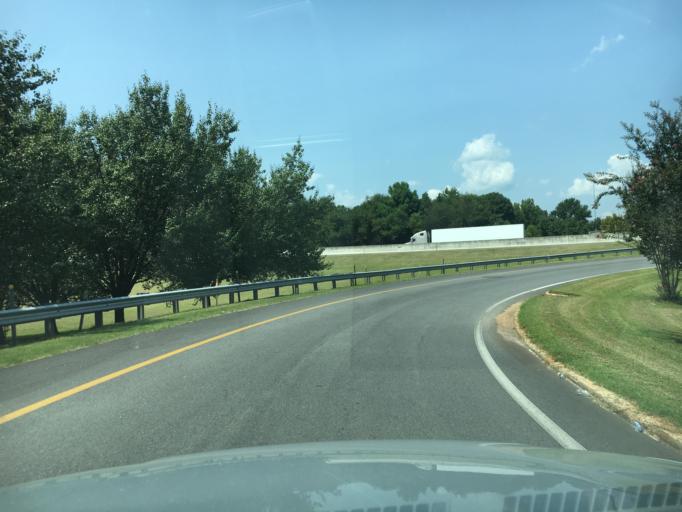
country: US
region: South Carolina
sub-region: Anderson County
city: Northlake
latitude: 34.5724
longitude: -82.7128
